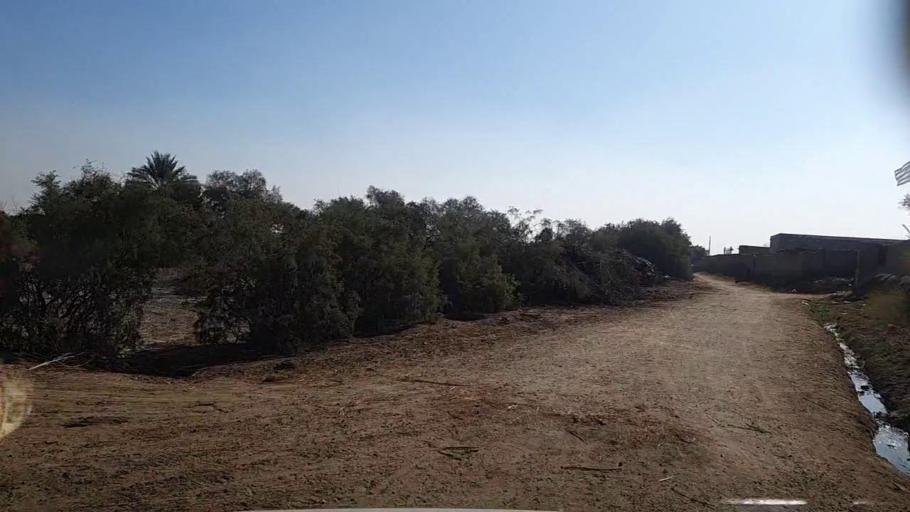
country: PK
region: Sindh
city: Khairpur
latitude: 27.9486
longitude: 69.7506
